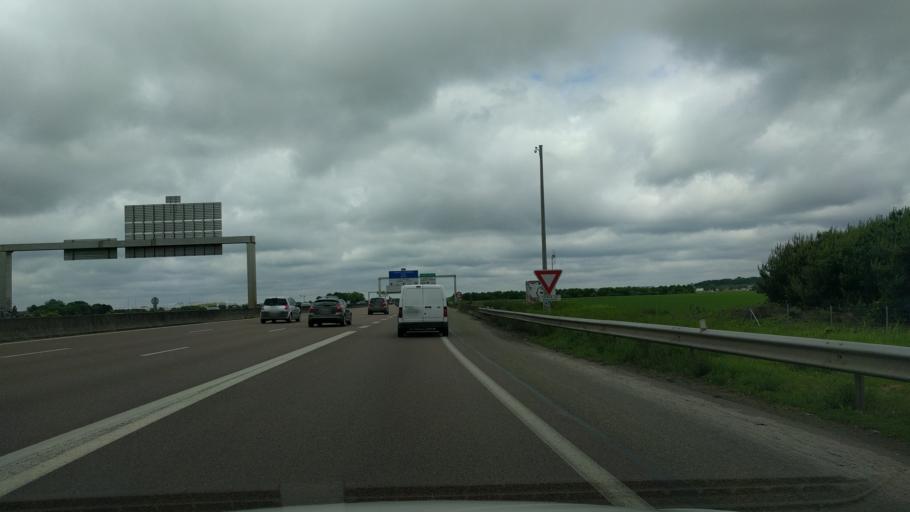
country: FR
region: Ile-de-France
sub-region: Departement de Seine-et-Marne
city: Nandy
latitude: 48.6117
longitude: 2.5715
